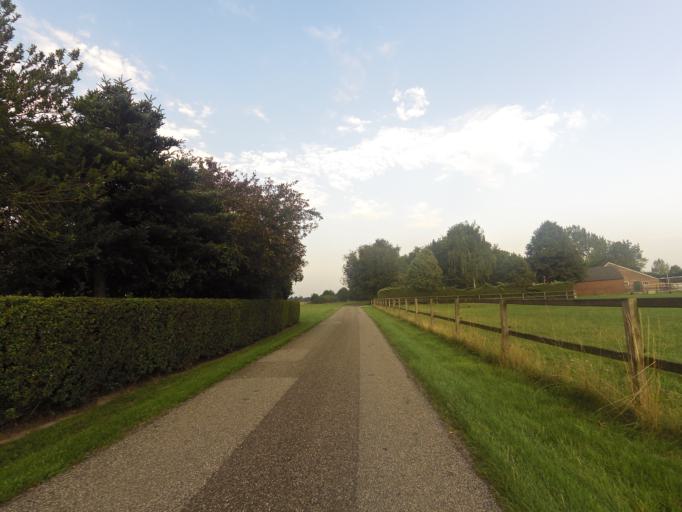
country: NL
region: Gelderland
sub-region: Oude IJsselstreek
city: Gendringen
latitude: 51.8836
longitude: 6.3569
